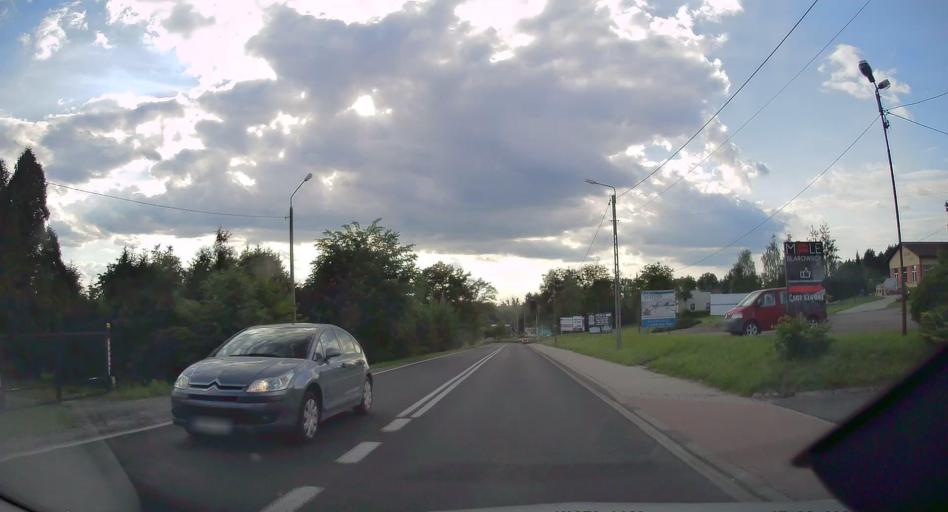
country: PL
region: Lesser Poland Voivodeship
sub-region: Powiat oswiecimski
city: Bulowice
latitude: 49.8745
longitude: 19.2940
